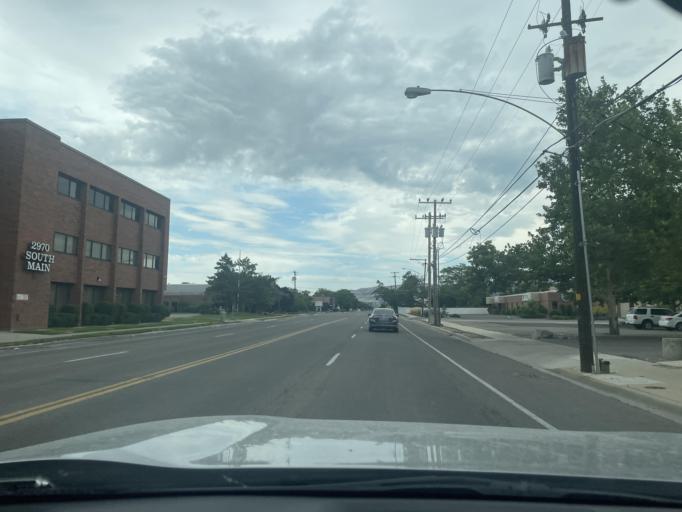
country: US
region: Utah
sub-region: Salt Lake County
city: South Salt Lake
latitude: 40.7065
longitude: -111.8911
